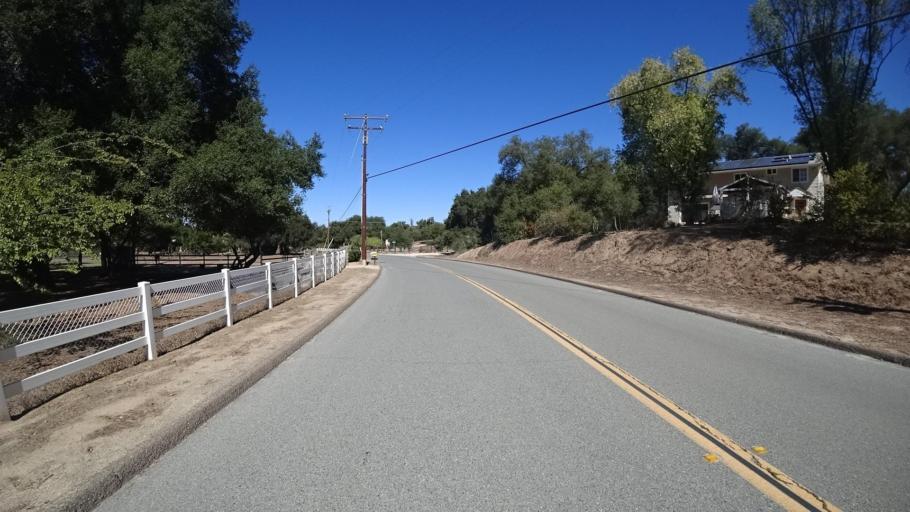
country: US
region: California
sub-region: San Diego County
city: Alpine
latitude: 32.7470
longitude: -116.7553
